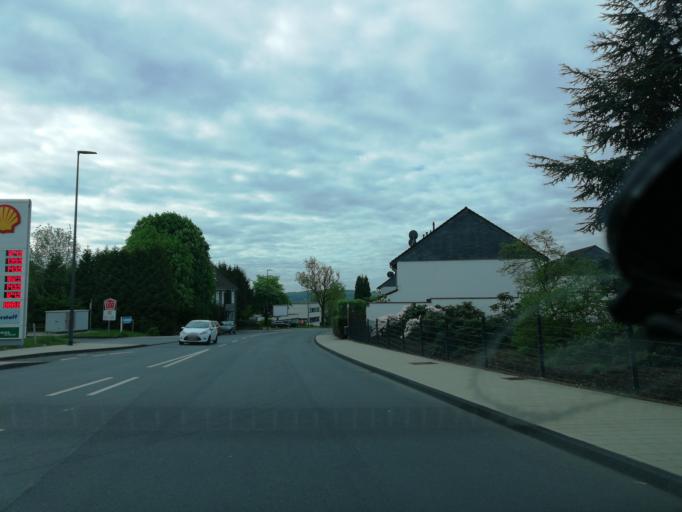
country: DE
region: North Rhine-Westphalia
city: Sprockhovel
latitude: 51.3083
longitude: 7.2520
